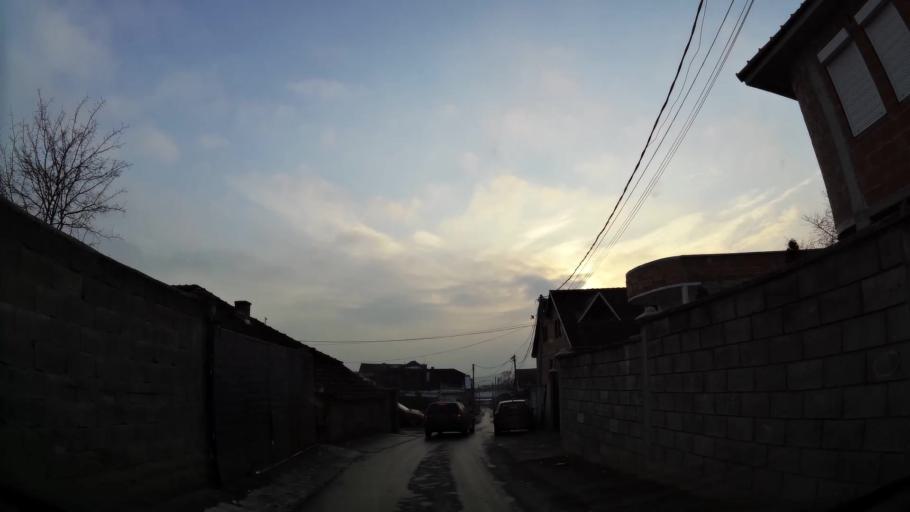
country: MK
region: Aracinovo
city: Arachinovo
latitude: 42.0252
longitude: 21.5617
